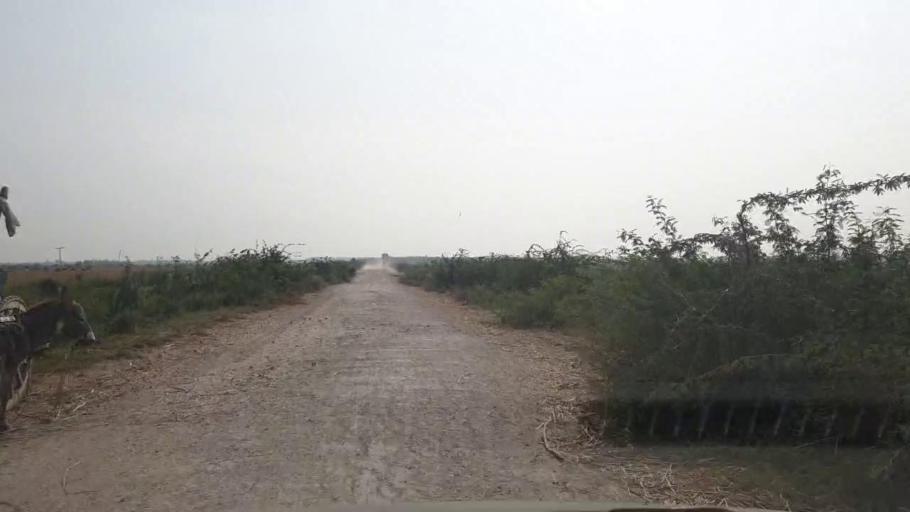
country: PK
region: Sindh
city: Tando Muhammad Khan
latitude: 25.0491
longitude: 68.3889
